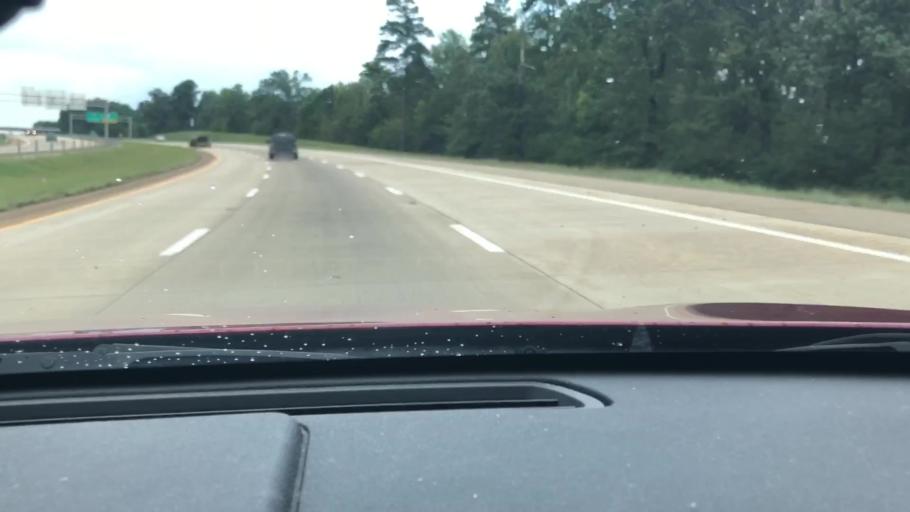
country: US
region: Texas
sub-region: Bowie County
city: Texarkana
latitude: 33.4039
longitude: -94.0052
